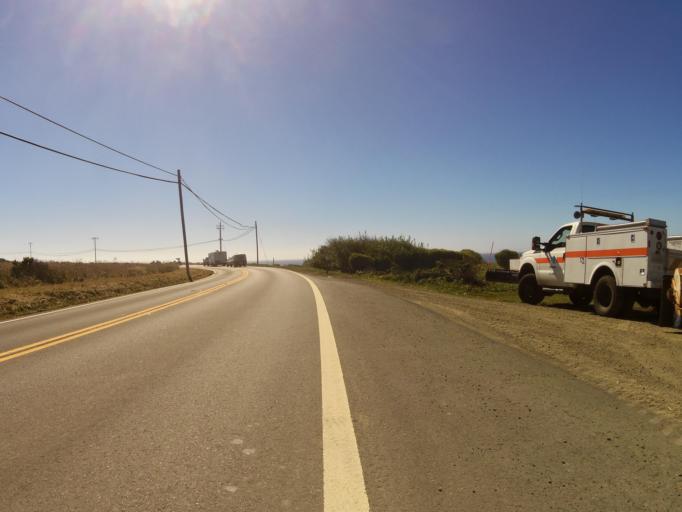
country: US
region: California
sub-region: Mendocino County
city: Fort Bragg
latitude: 39.6480
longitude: -123.7836
